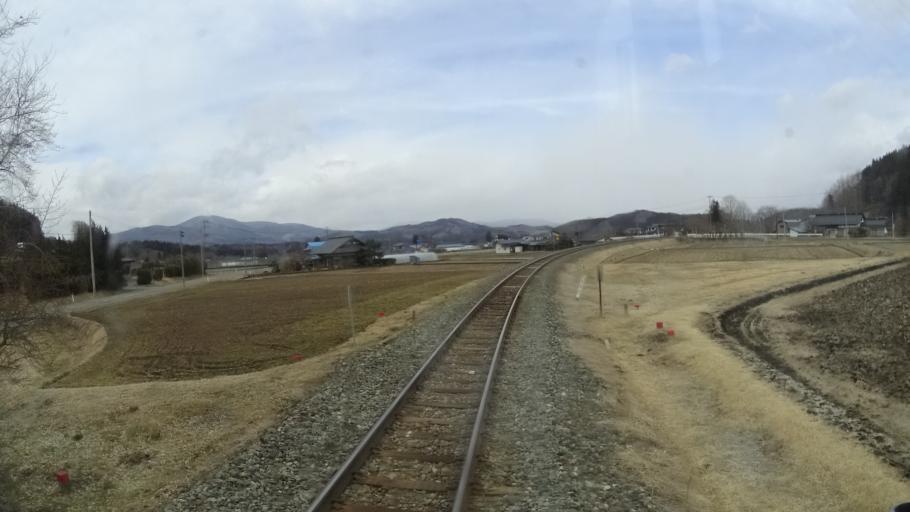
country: JP
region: Iwate
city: Tono
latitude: 39.2663
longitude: 141.5892
